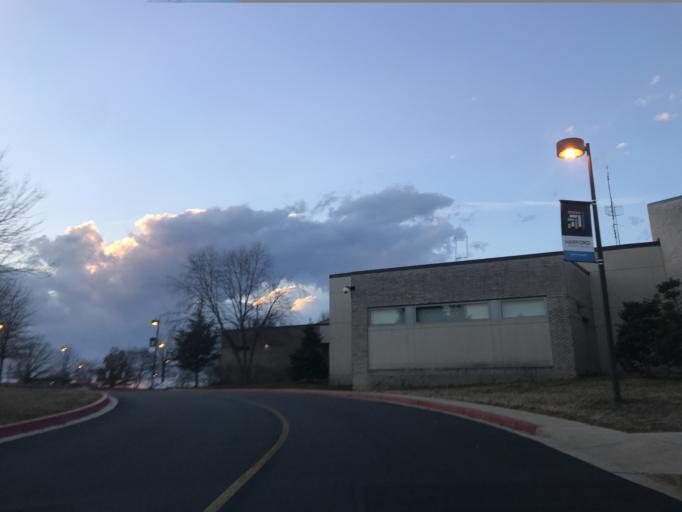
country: US
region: Maryland
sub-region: Harford County
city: South Bel Air
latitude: 39.5633
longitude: -76.2862
